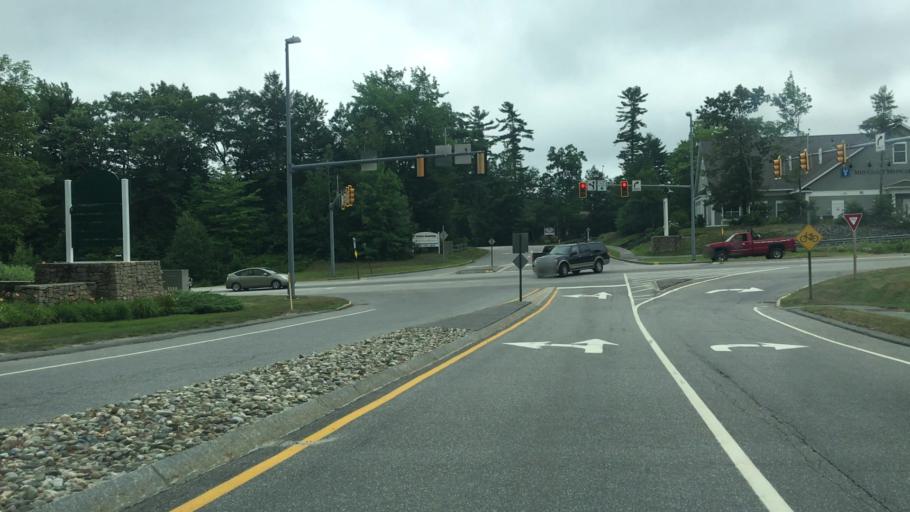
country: US
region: Maine
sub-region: Sagadahoc County
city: Topsham
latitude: 43.9364
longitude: -69.9564
